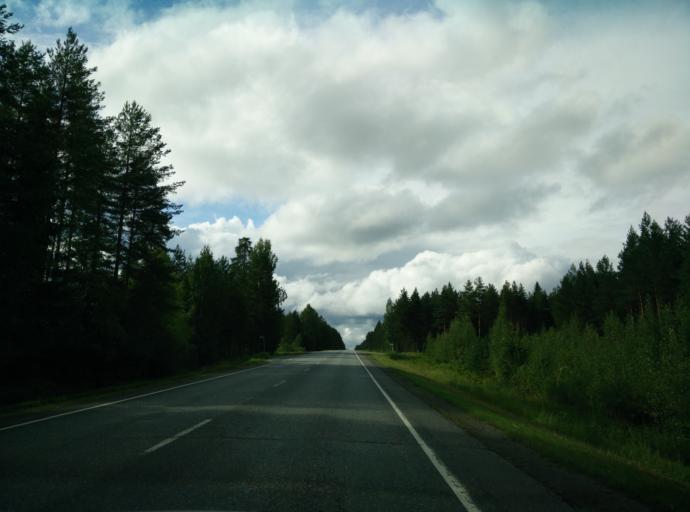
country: FI
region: Haeme
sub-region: Haemeenlinna
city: Kalvola
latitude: 61.1084
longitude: 24.1308
